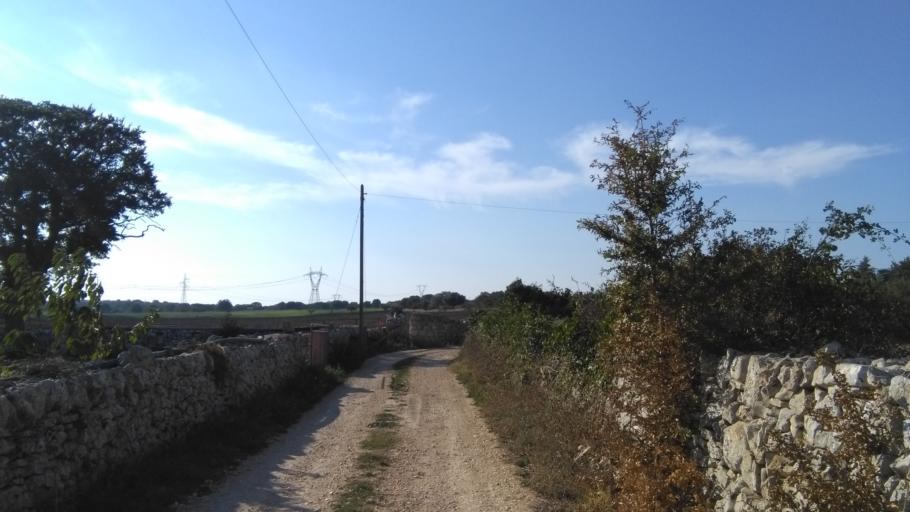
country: IT
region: Apulia
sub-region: Provincia di Bari
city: Putignano
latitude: 40.8219
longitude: 17.0564
